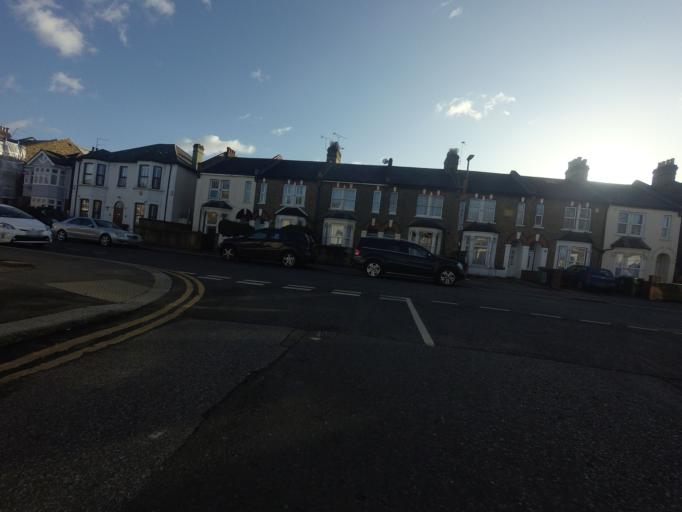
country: GB
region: England
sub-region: Greater London
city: East Ham
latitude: 51.5513
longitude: 0.0318
